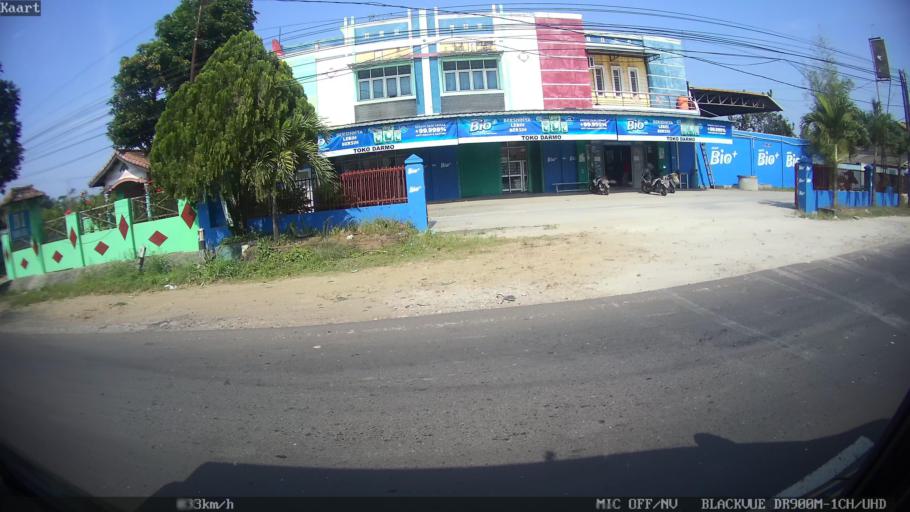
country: ID
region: Lampung
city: Natar
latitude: -5.2337
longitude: 105.1725
